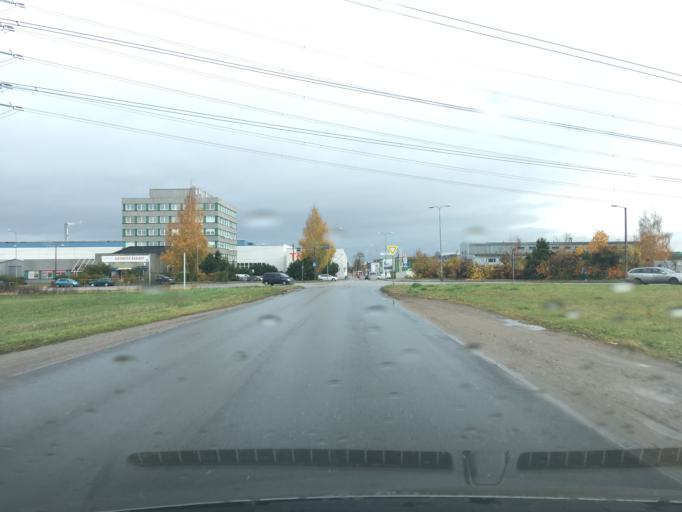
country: EE
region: Tartu
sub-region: Tartu linn
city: Tartu
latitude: 58.3811
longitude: 26.6836
